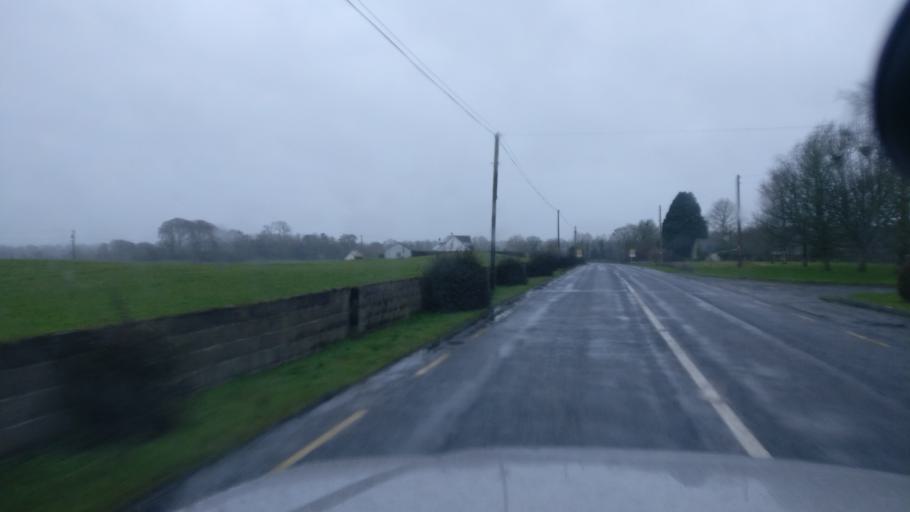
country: IE
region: Connaught
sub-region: County Galway
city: Portumna
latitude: 53.1484
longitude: -8.1955
